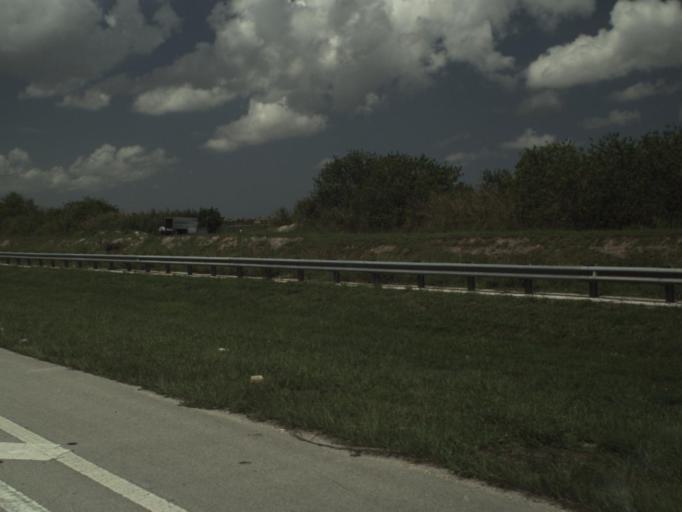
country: US
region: Florida
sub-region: Palm Beach County
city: Villages of Oriole
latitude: 26.4174
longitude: -80.2040
